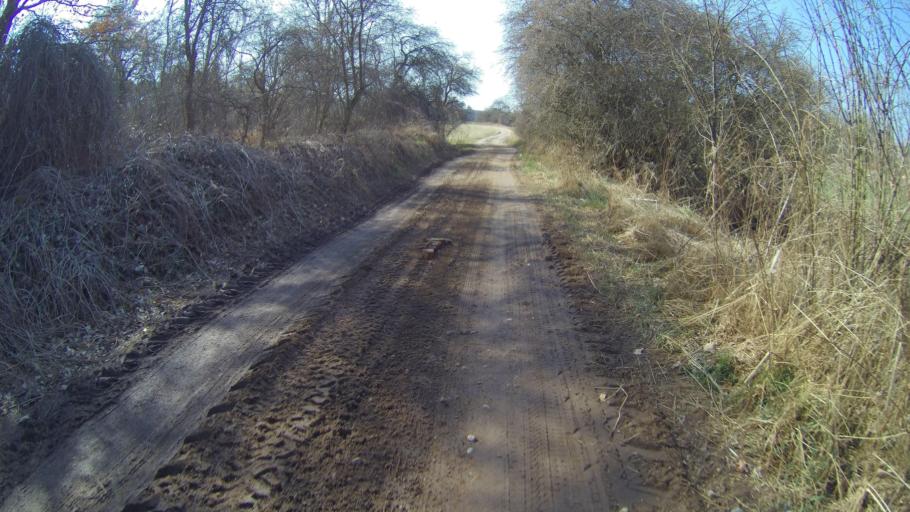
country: CZ
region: Ustecky
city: Mecholupy
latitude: 50.2714
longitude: 13.5653
